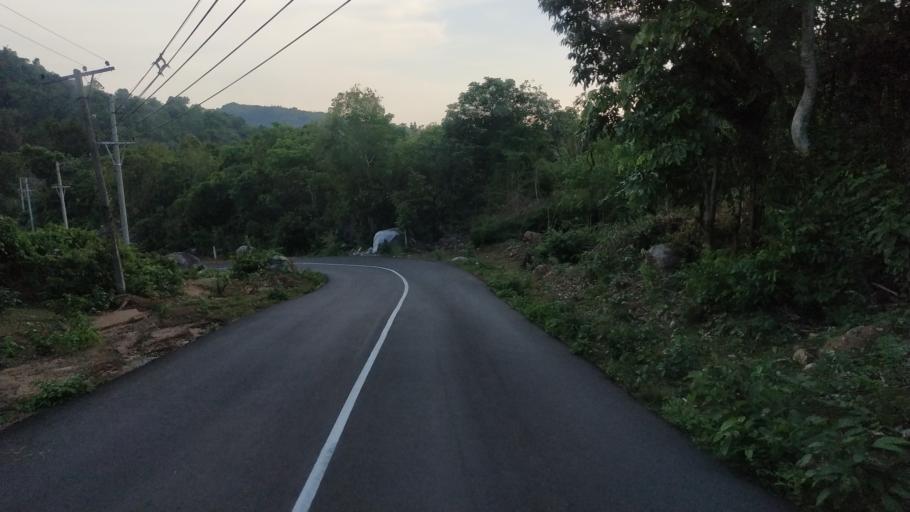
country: MM
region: Mon
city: Kyaikto
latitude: 17.4337
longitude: 97.0942
